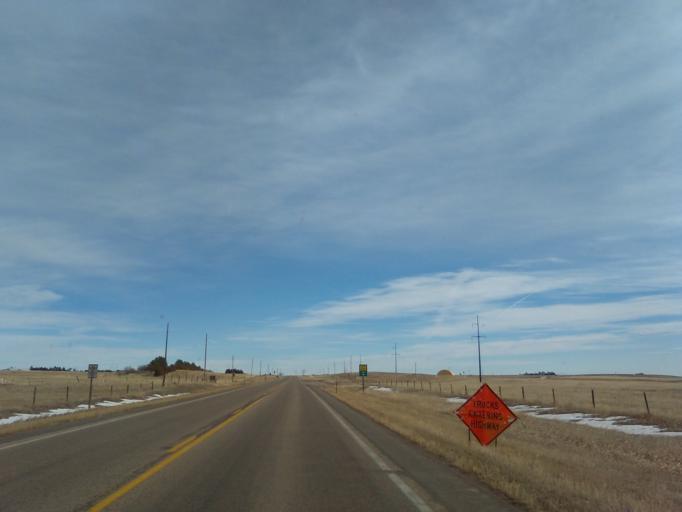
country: US
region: Wyoming
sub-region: Laramie County
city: Pine Bluffs
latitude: 41.4184
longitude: -104.4112
